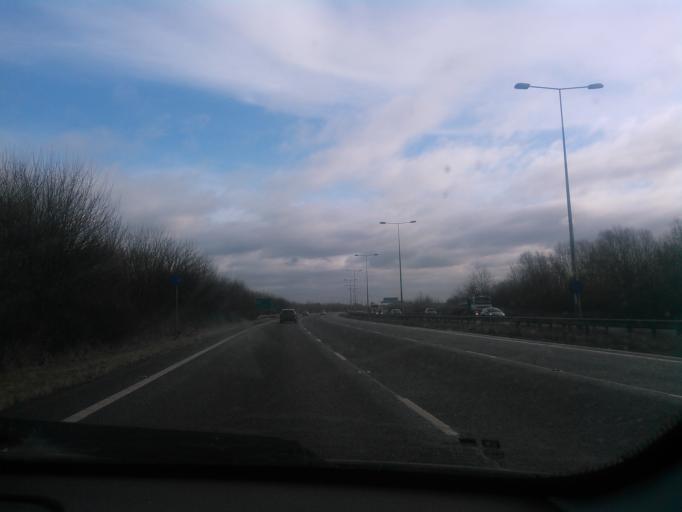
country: GB
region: England
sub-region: Derbyshire
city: Borrowash
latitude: 52.8712
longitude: -1.3792
